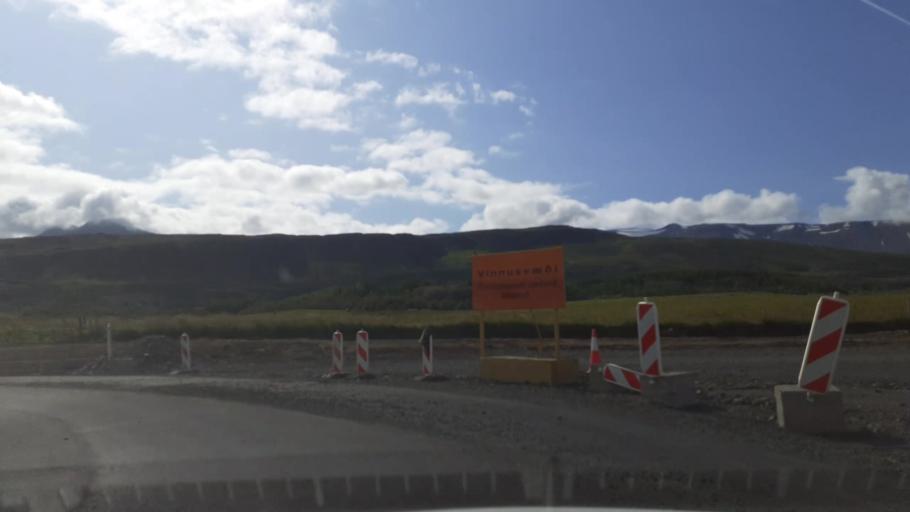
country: IS
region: Northeast
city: Akureyri
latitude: 65.6562
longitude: -18.0965
